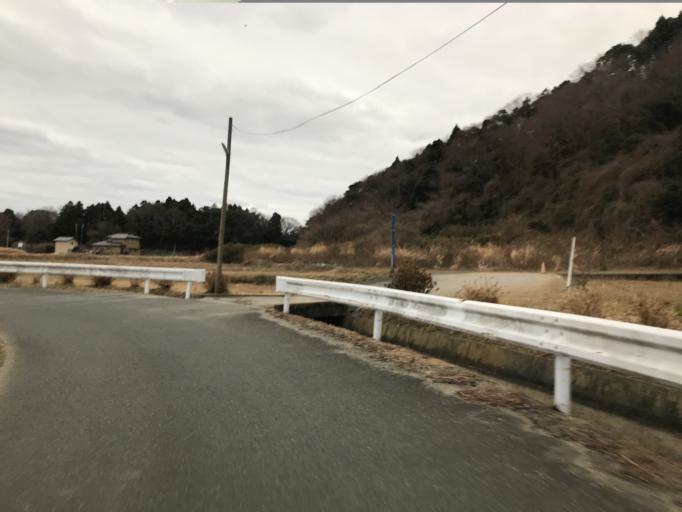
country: JP
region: Fukushima
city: Iwaki
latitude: 37.0466
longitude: 140.9548
